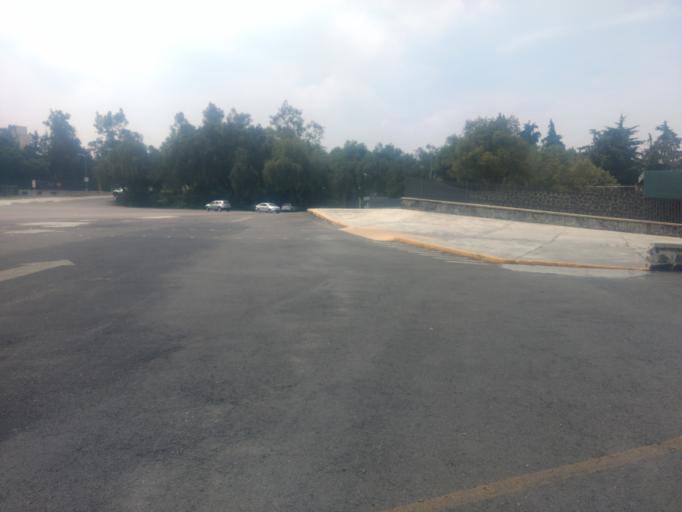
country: MX
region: Mexico City
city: Magdalena Contreras
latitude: 19.3304
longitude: -99.1911
